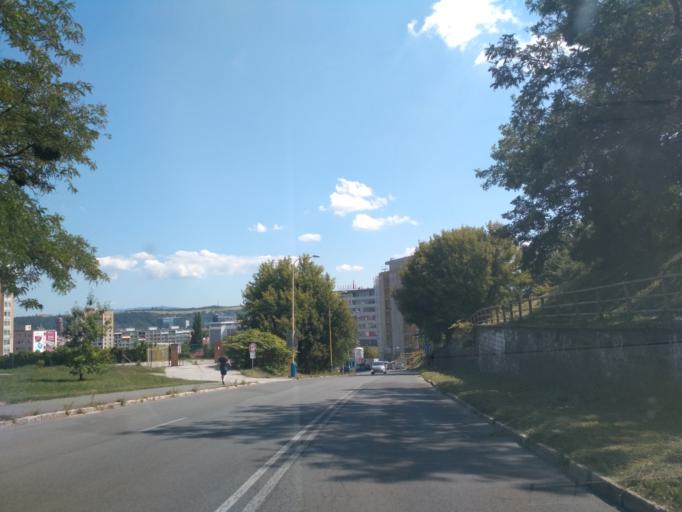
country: SK
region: Kosicky
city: Kosice
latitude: 48.7199
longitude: 21.2427
